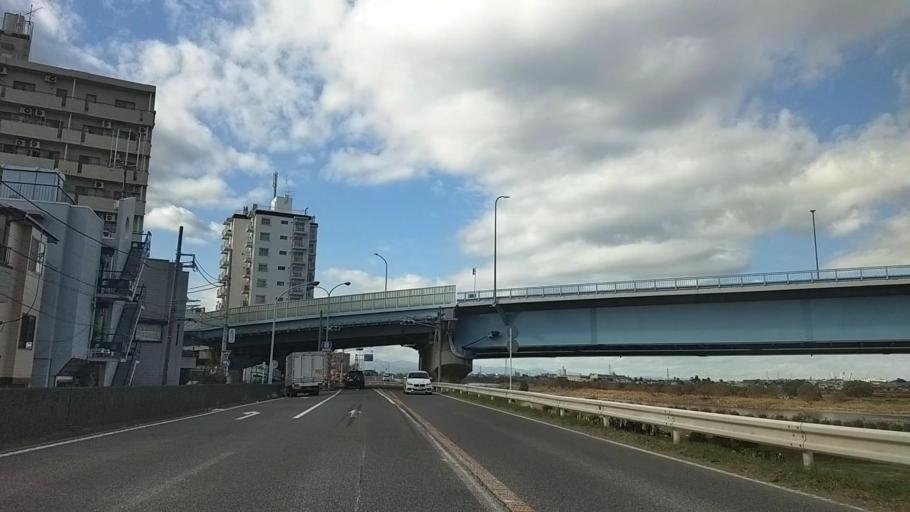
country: JP
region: Tokyo
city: Chofugaoka
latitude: 35.6097
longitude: 139.6195
